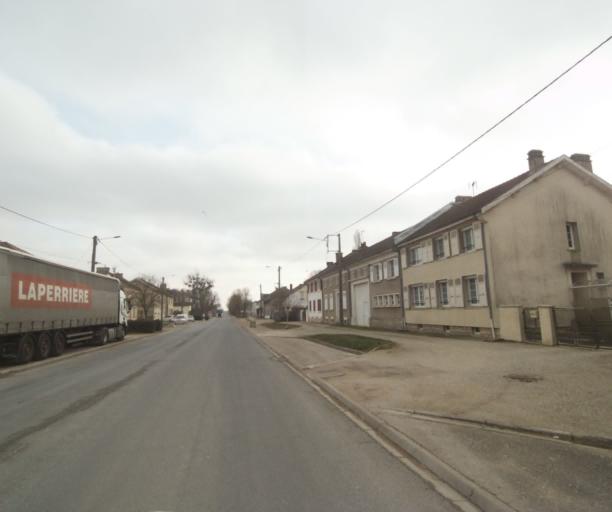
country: FR
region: Champagne-Ardenne
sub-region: Departement de la Haute-Marne
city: Villiers-en-Lieu
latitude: 48.6548
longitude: 4.8259
